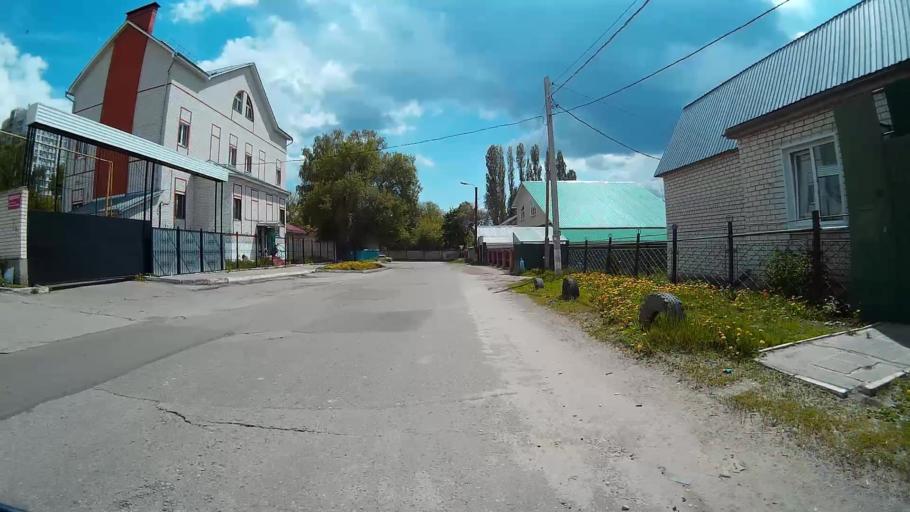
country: RU
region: Ulyanovsk
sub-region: Ulyanovskiy Rayon
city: Ulyanovsk
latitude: 54.3374
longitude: 48.3795
